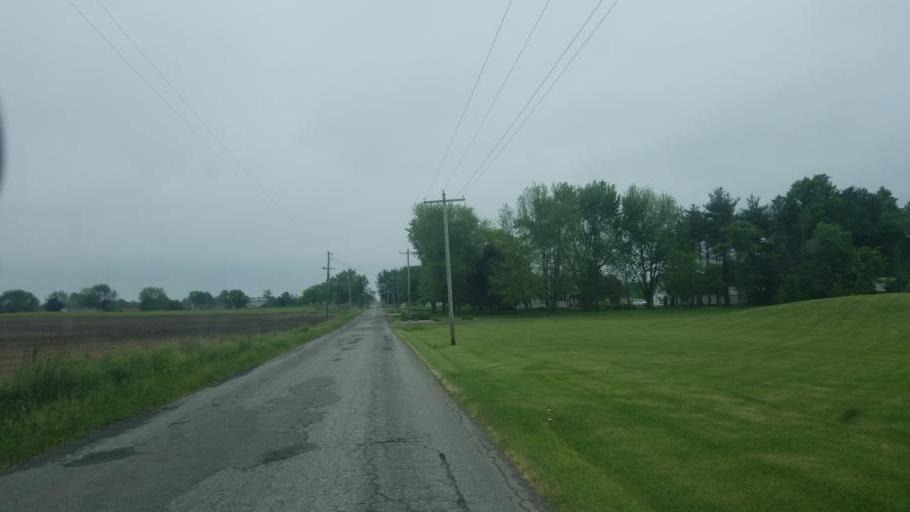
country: US
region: Indiana
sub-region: Marshall County
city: Bremen
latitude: 41.4590
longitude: -86.1176
